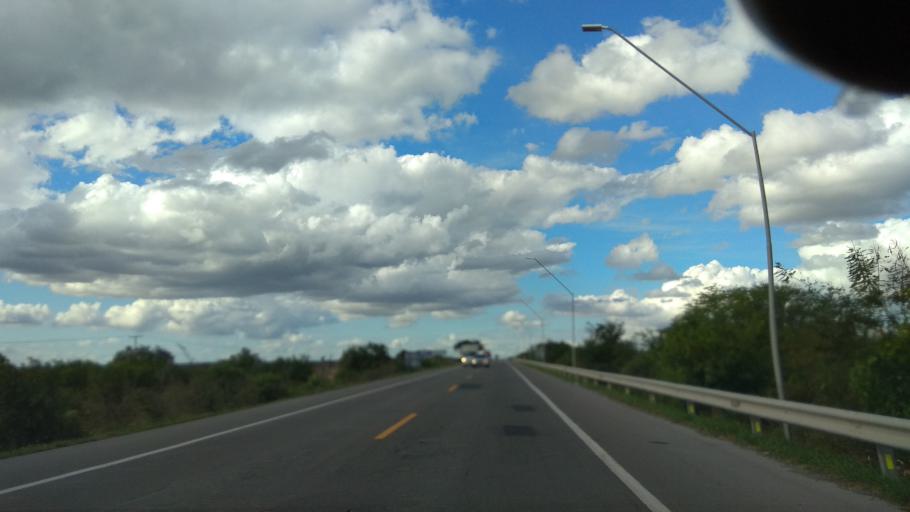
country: BR
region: Bahia
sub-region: Castro Alves
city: Castro Alves
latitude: -12.6096
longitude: -39.5621
